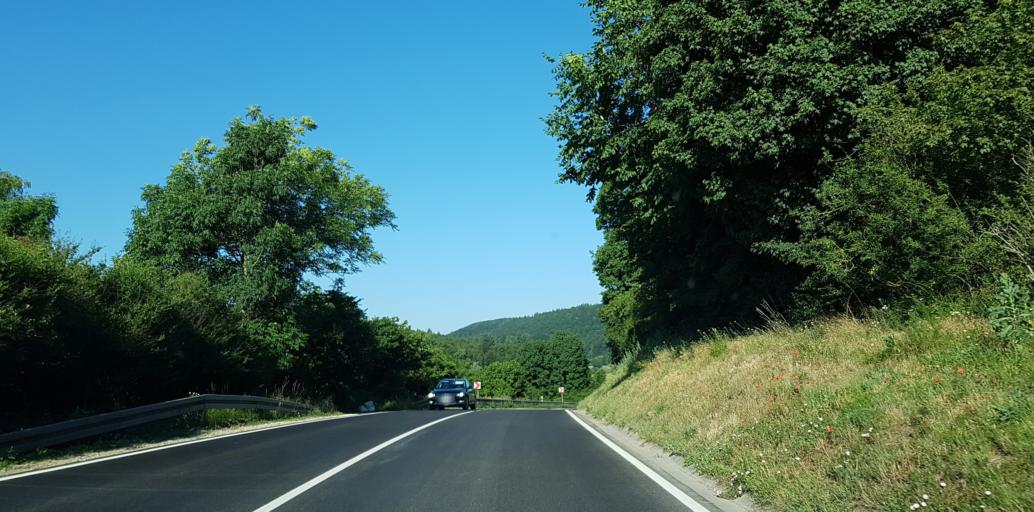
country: DE
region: Baden-Wuerttemberg
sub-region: Tuebingen Region
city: Blaubeuren
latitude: 48.4097
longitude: 9.8541
